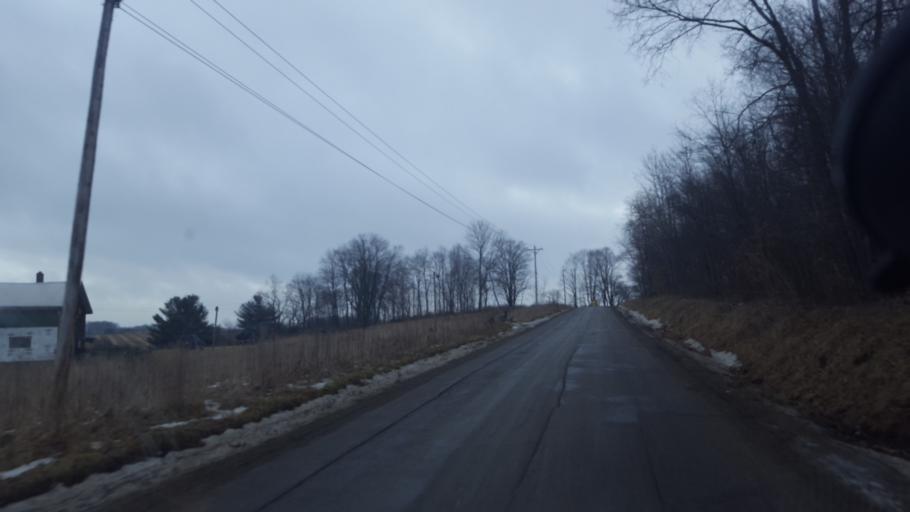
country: US
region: New York
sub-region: Allegany County
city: Andover
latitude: 41.9860
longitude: -77.7474
